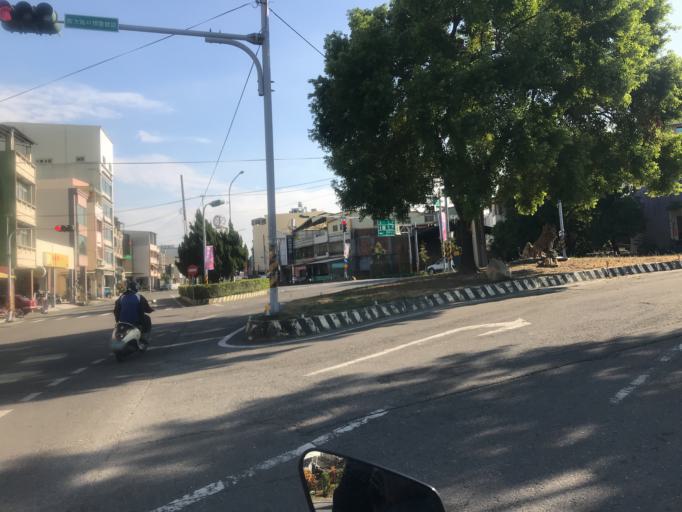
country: TW
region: Taiwan
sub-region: Nantou
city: Nantou
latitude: 23.8553
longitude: 120.5872
